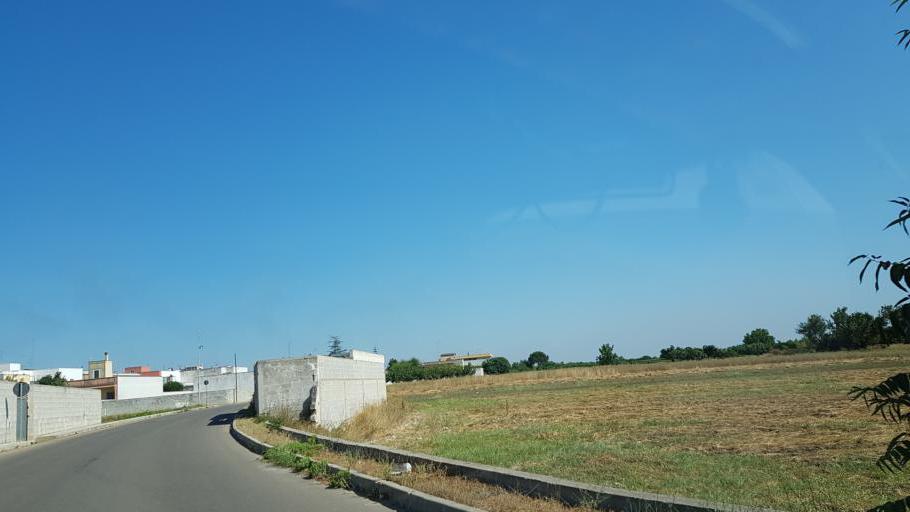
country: IT
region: Apulia
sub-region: Provincia di Brindisi
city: San Donaci
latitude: 40.4442
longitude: 17.9232
